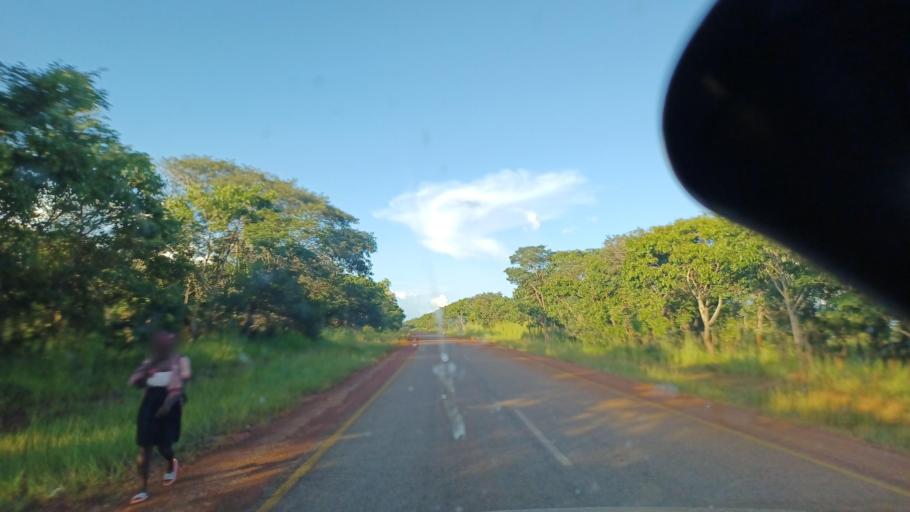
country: ZM
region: North-Western
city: Kalengwa
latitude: -13.1392
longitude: 25.0695
